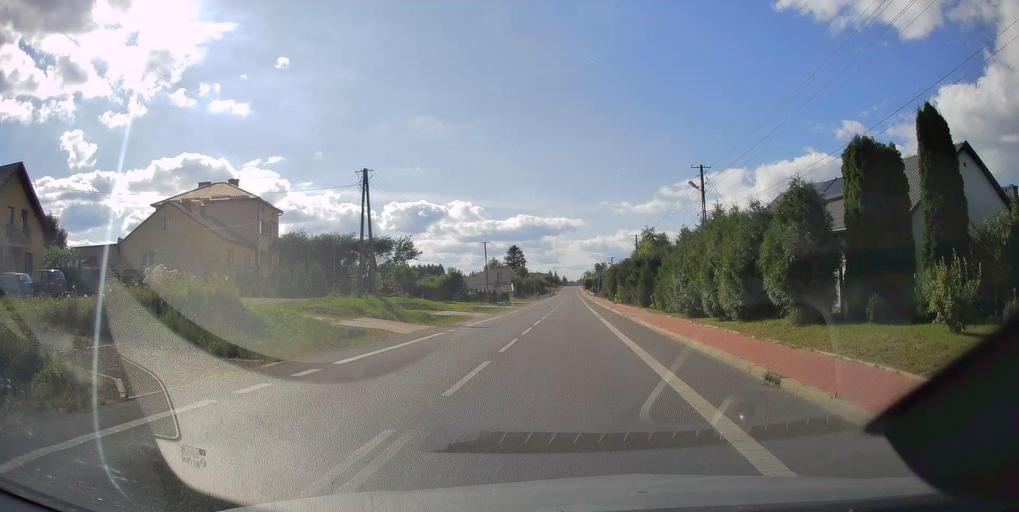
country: PL
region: Swietokrzyskie
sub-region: Powiat kielecki
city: Bodzentyn
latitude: 50.9332
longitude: 20.9682
